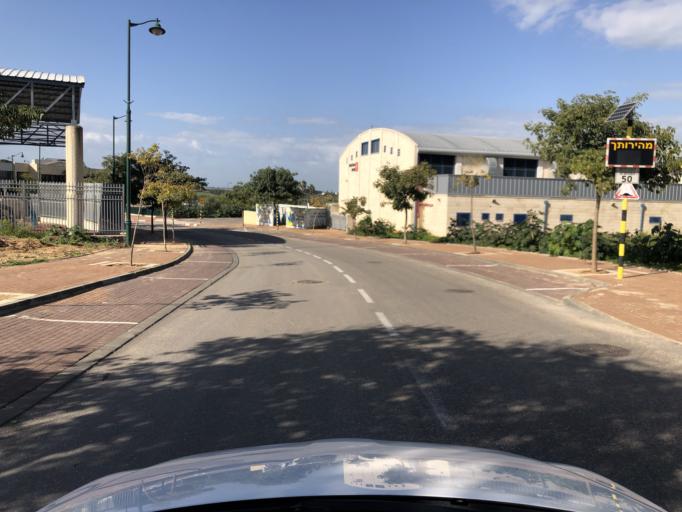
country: IL
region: Central District
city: Ness Ziona
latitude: 31.9095
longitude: 34.7859
